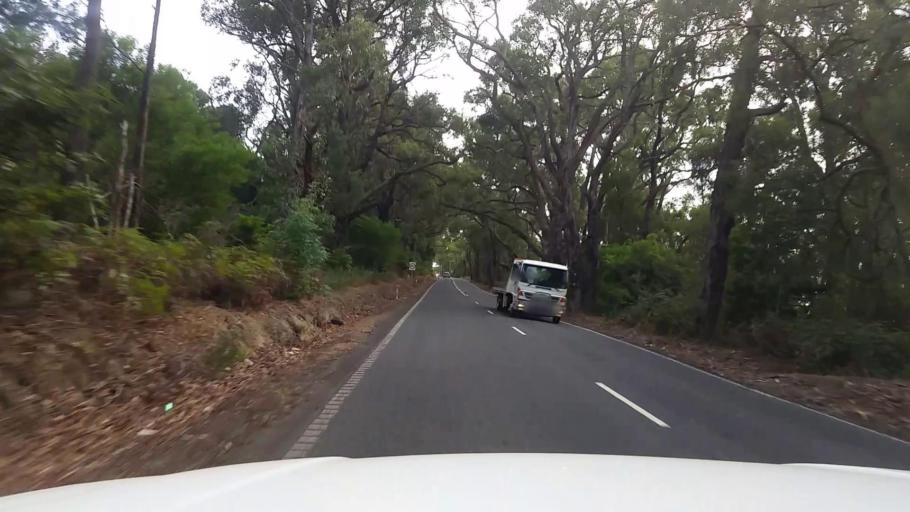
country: AU
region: Victoria
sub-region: Mornington Peninsula
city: Balnarring
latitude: -38.3356
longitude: 145.0959
